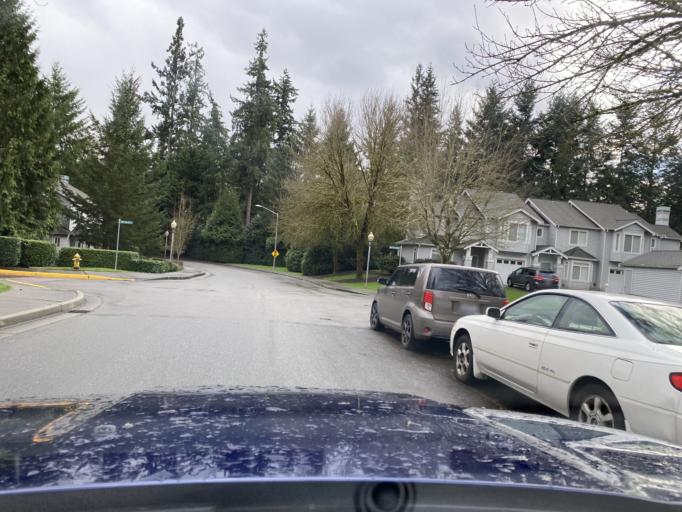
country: US
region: Washington
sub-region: King County
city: Redmond
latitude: 47.6838
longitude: -122.1008
